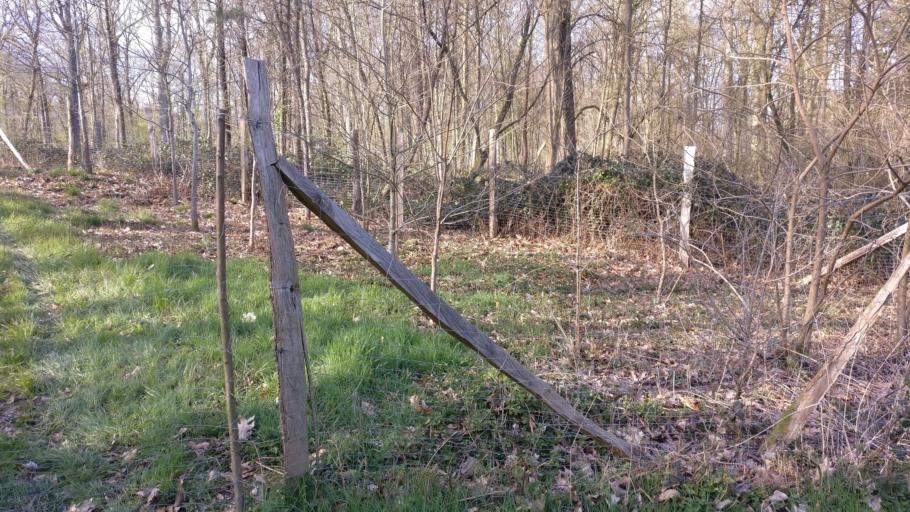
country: BE
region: Flanders
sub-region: Provincie Vlaams-Brabant
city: Tervuren
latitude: 50.8078
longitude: 4.5045
